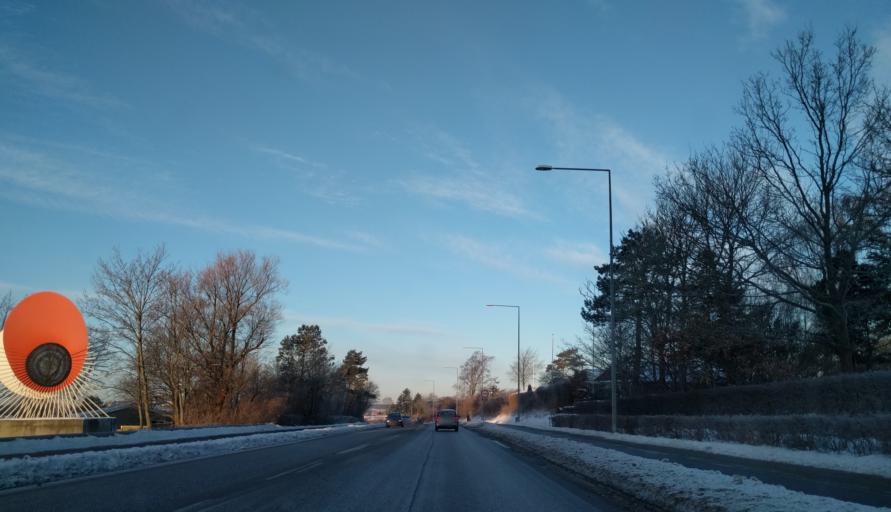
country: DK
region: North Denmark
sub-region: Alborg Kommune
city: Aalborg
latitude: 57.0253
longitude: 9.9395
